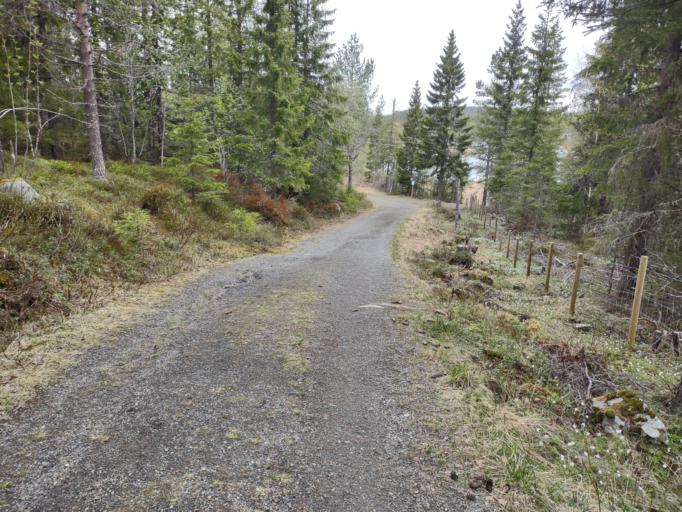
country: NO
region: Oppland
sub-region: Gran
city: Jaren
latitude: 60.4521
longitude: 10.6452
